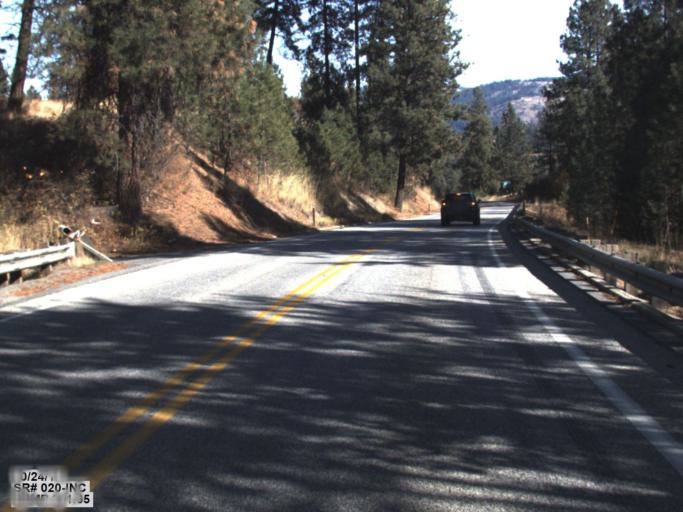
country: US
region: Washington
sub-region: Stevens County
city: Kettle Falls
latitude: 48.6230
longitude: -118.1286
